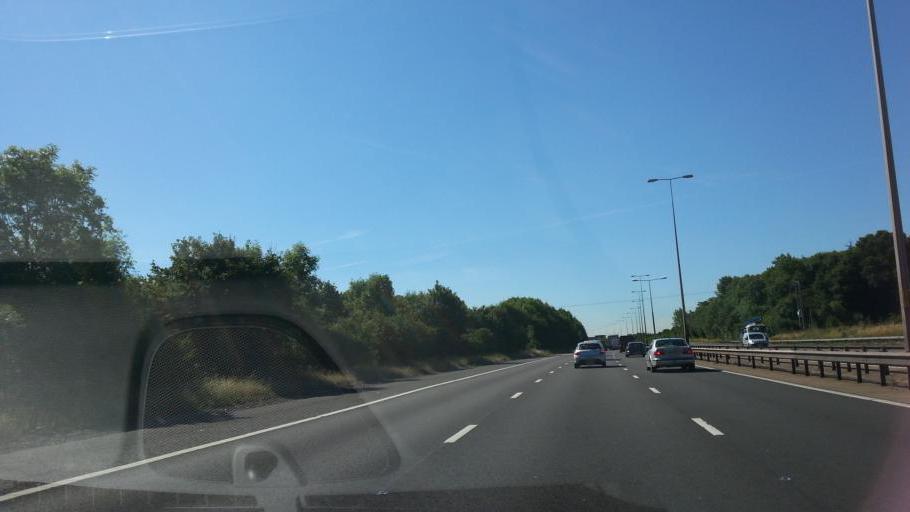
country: GB
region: England
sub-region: Worcestershire
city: Upton upon Severn
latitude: 52.0997
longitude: -2.1869
